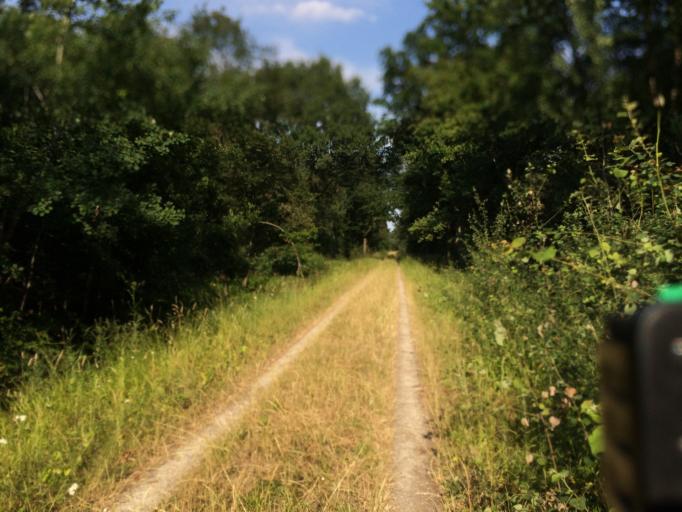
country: FR
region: Ile-de-France
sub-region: Departement de l'Essonne
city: Brunoy
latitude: 48.6670
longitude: 2.4892
